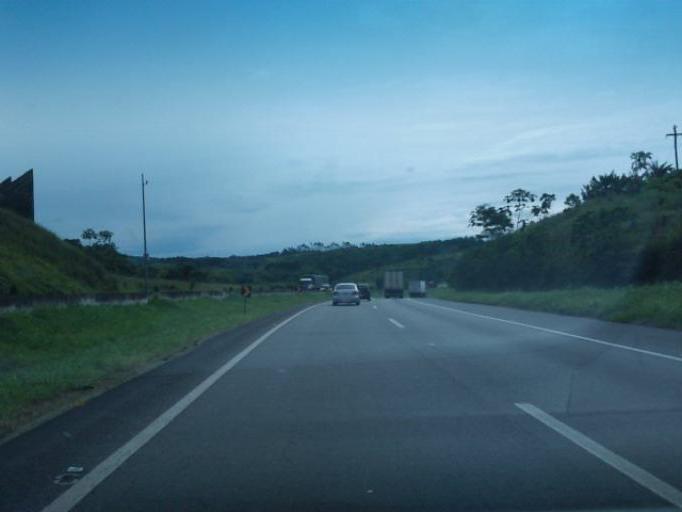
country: BR
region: Sao Paulo
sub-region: Cajati
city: Cajati
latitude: -24.7404
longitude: -48.1248
